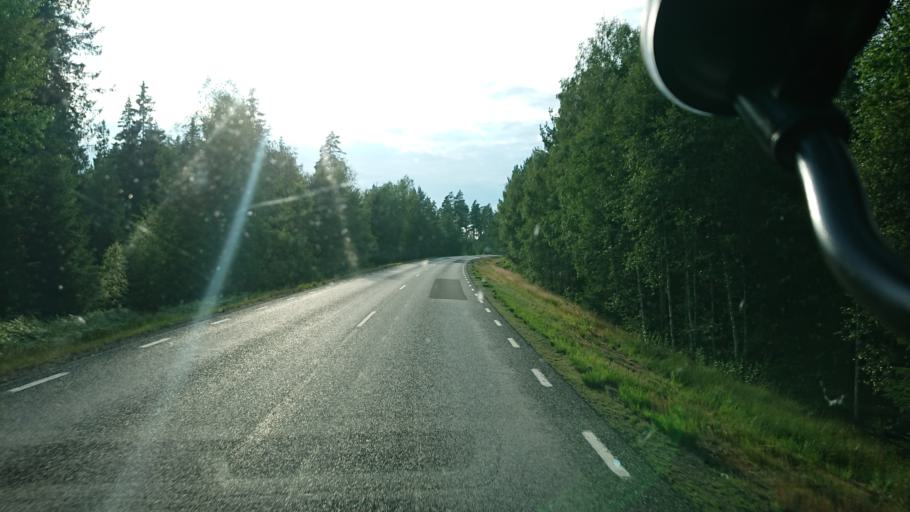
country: SE
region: Kronoberg
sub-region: Vaxjo Kommun
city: Braas
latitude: 57.0262
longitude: 14.9822
